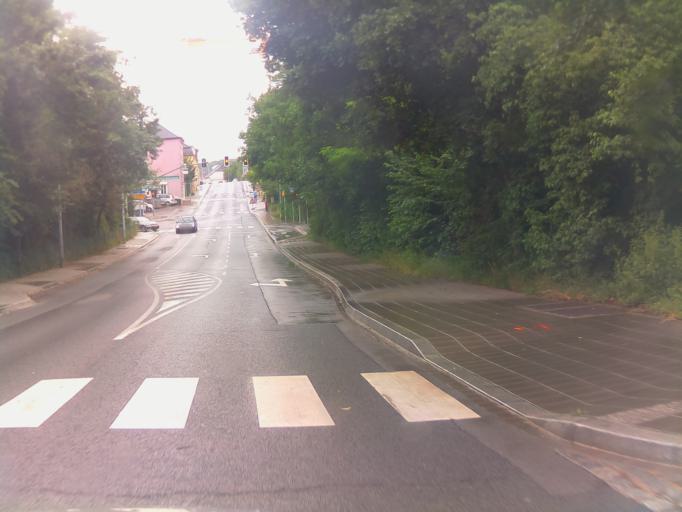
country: LU
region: Luxembourg
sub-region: Canton d'Esch-sur-Alzette
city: Sanem
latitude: 49.5470
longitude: 5.9299
